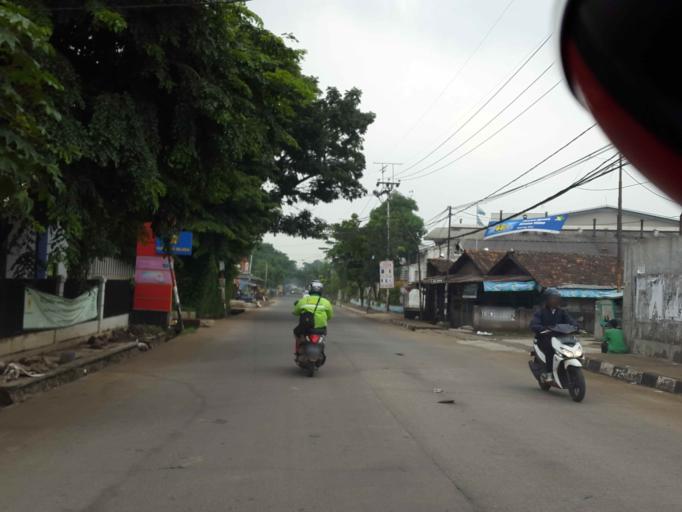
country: ID
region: West Java
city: Cimahi
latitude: -6.8983
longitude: 107.5543
